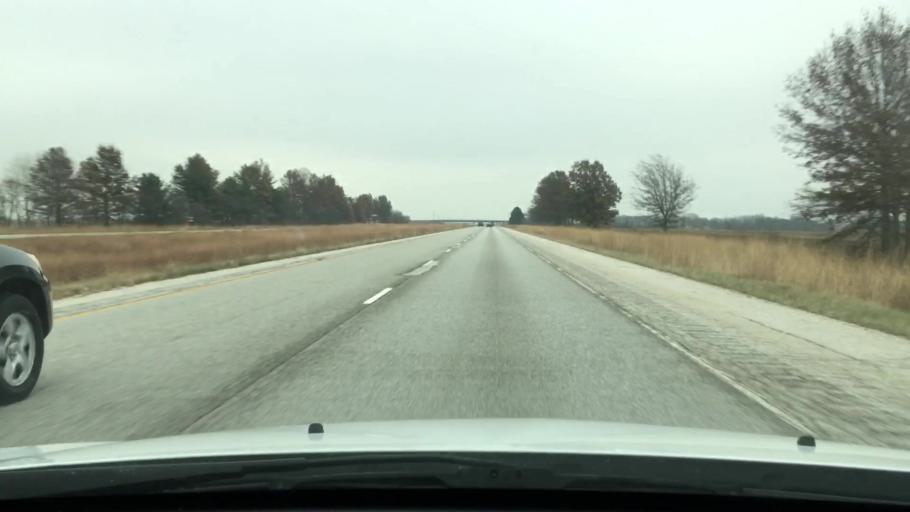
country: US
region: Illinois
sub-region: Morgan County
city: Jacksonville
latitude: 39.7376
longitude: -90.1379
